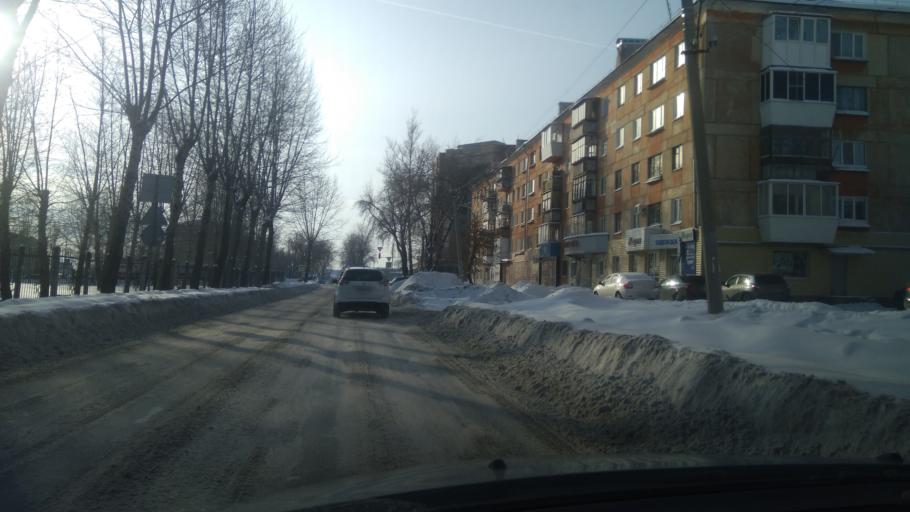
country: RU
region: Sverdlovsk
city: Sukhoy Log
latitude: 56.9010
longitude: 62.0295
